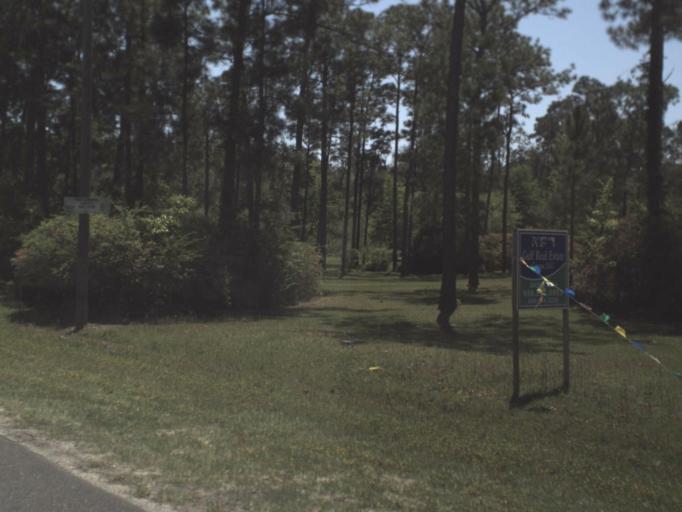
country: US
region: Florida
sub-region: Escambia County
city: Ensley
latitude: 30.5101
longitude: -87.3086
